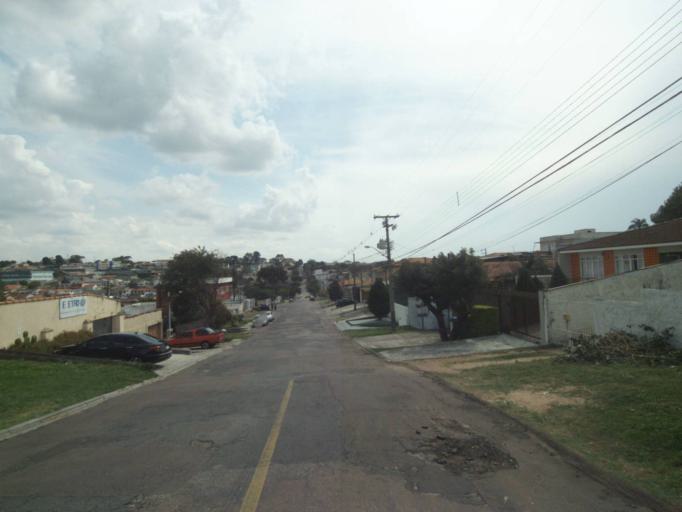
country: BR
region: Parana
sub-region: Pinhais
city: Pinhais
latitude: -25.4030
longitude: -49.2058
